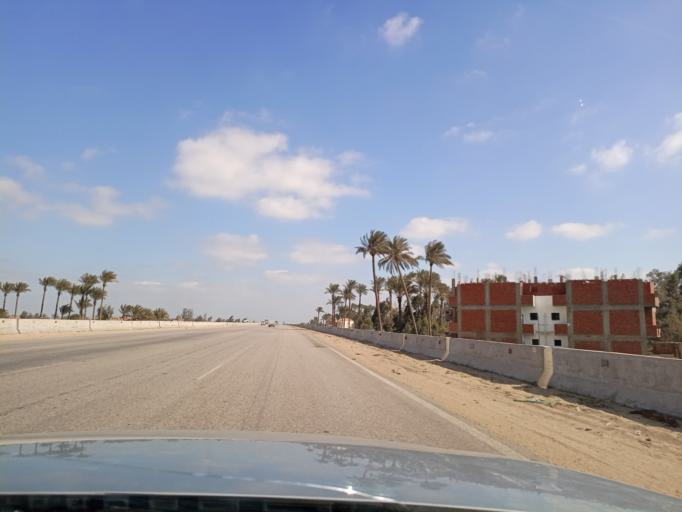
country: EG
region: Muhafazat al Qalyubiyah
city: Banha
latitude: 30.4452
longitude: 31.1194
